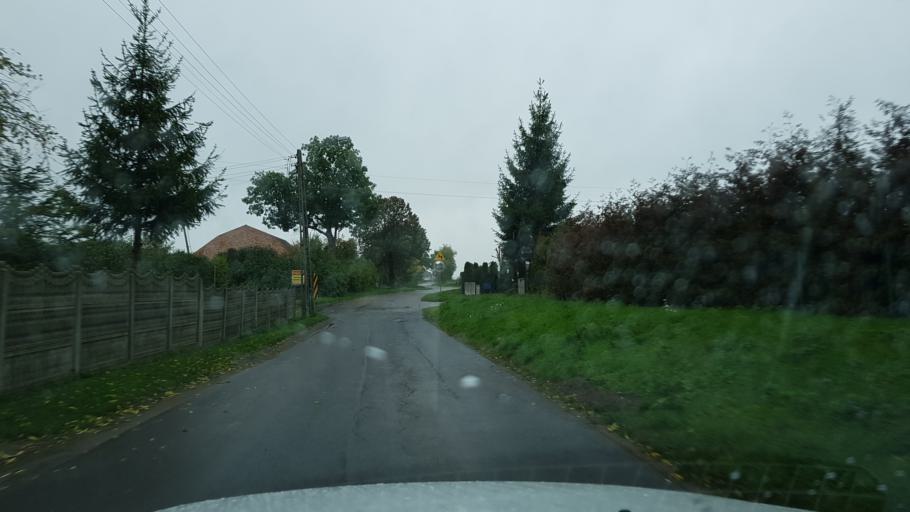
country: PL
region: West Pomeranian Voivodeship
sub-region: Powiat pyrzycki
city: Pyrzyce
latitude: 53.1612
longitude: 14.8404
